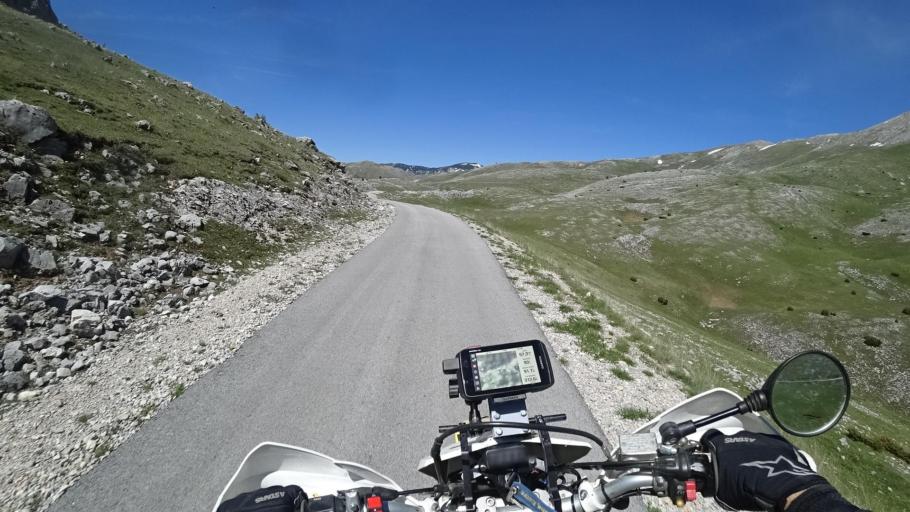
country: BA
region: Federation of Bosnia and Herzegovina
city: Gracanica
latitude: 43.6864
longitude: 18.2505
